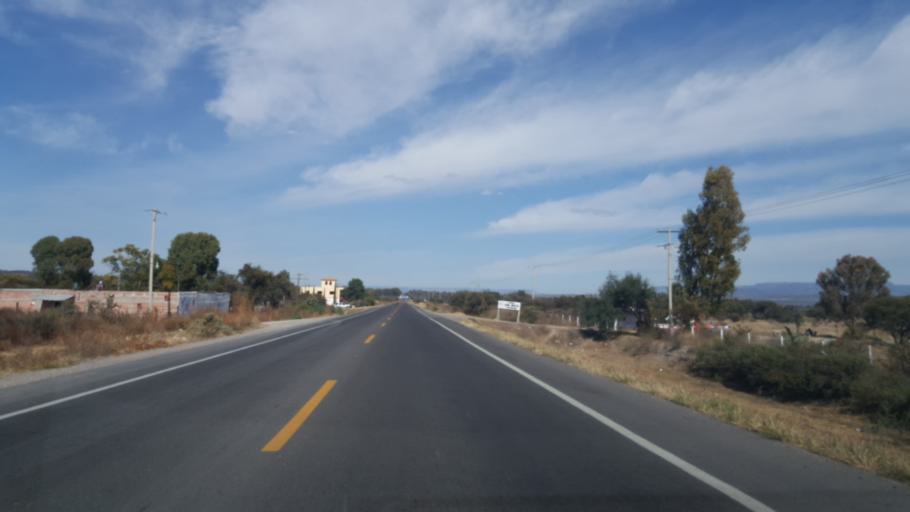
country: MX
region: Jalisco
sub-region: Lagos de Moreno
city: Cristeros [Fraccionamiento]
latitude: 21.2621
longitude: -101.9464
